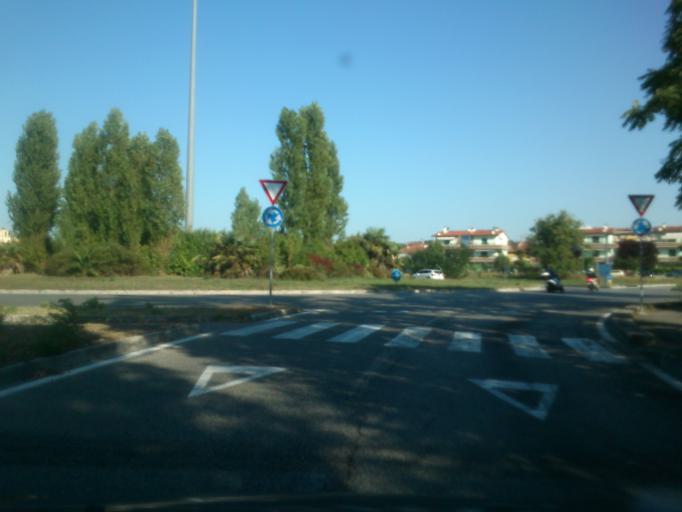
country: IT
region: The Marches
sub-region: Provincia di Pesaro e Urbino
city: Pesaro
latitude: 43.8894
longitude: 12.8992
